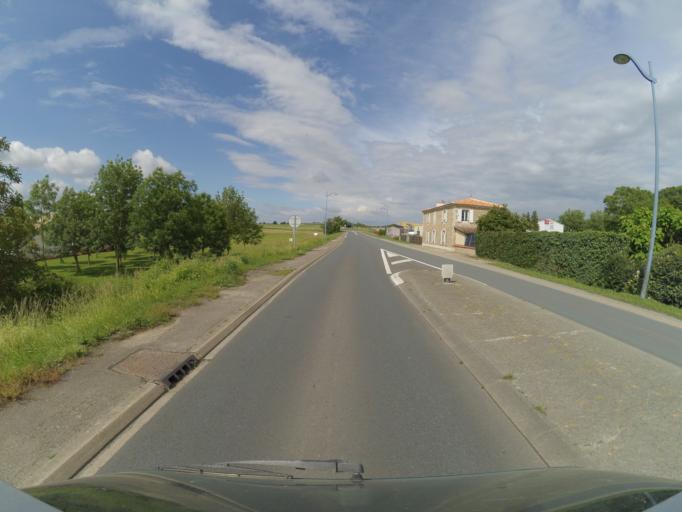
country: FR
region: Pays de la Loire
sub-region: Departement de la Vendee
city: Sainte-Hermine
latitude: 46.5238
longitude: -1.0825
